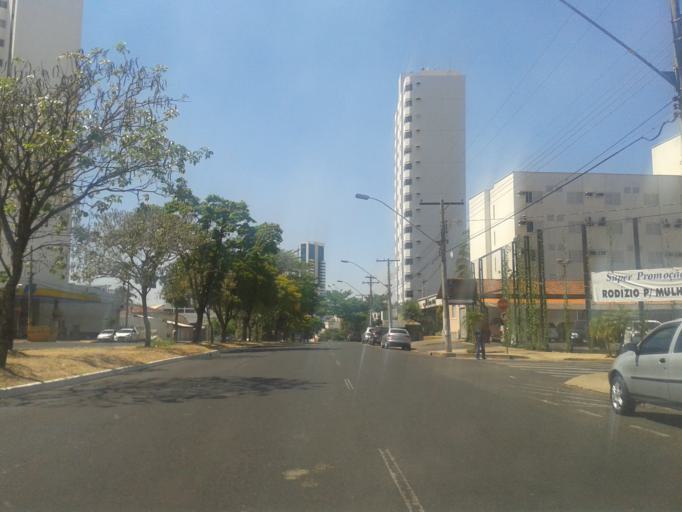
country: BR
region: Minas Gerais
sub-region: Uberlandia
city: Uberlandia
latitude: -18.9134
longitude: -48.2668
